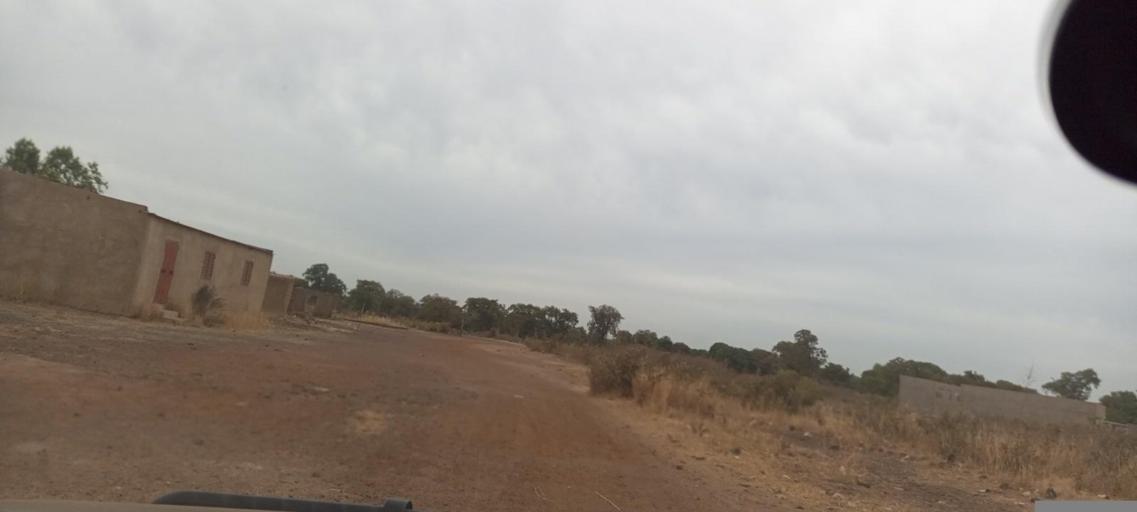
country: ML
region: Koulikoro
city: Kati
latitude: 12.7961
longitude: -8.2511
